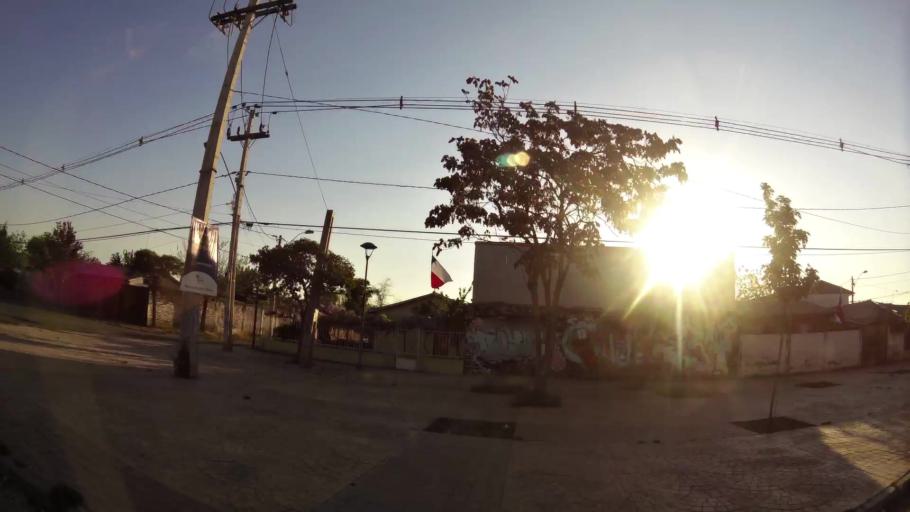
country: CL
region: Santiago Metropolitan
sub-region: Provincia de Santiago
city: La Pintana
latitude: -33.5425
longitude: -70.6181
